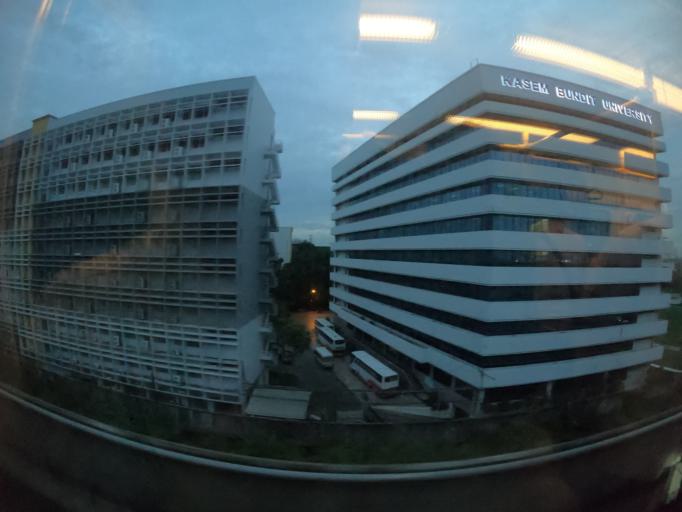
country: TH
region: Bangkok
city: Suan Luang
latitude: 13.7399
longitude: 100.6267
